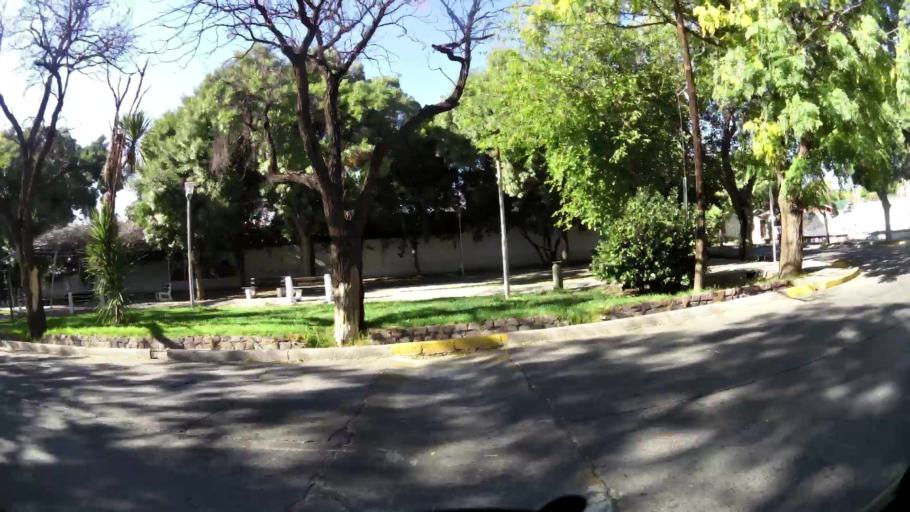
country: AR
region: Mendoza
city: Las Heras
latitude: -32.8704
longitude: -68.8538
